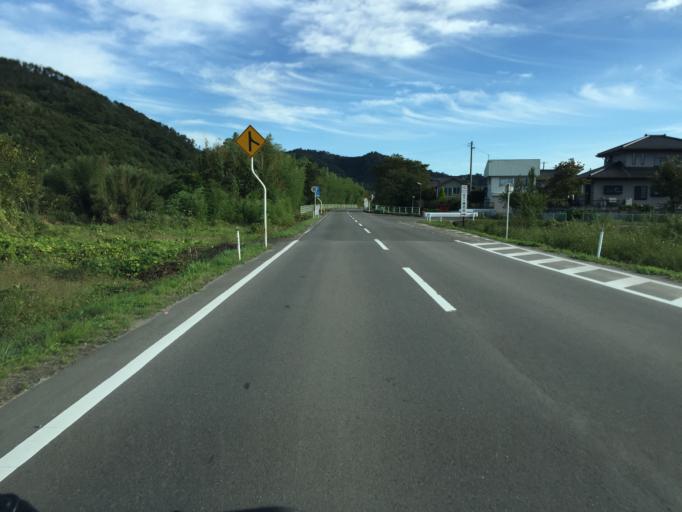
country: JP
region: Fukushima
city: Yanagawamachi-saiwaicho
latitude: 37.8235
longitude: 140.6172
